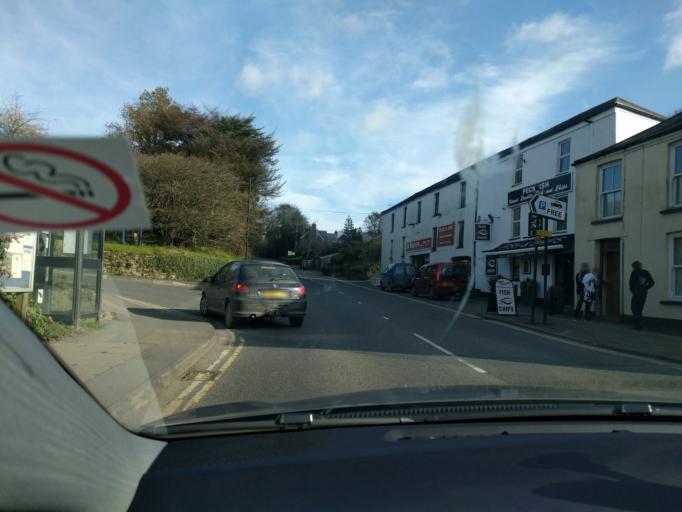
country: GB
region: England
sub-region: Cornwall
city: Camelford
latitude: 50.6233
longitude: -4.6776
